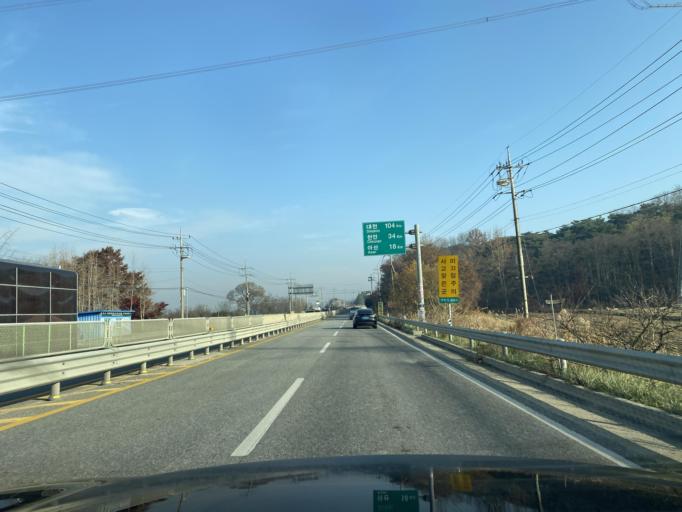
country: KR
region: Chungcheongnam-do
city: Yesan
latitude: 36.7416
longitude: 126.8600
